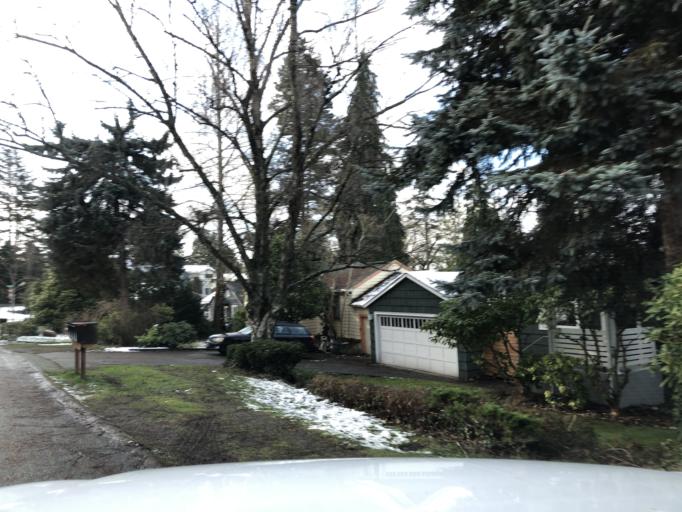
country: US
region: Washington
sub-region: King County
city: Lake Forest Park
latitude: 47.7310
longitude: -122.2897
